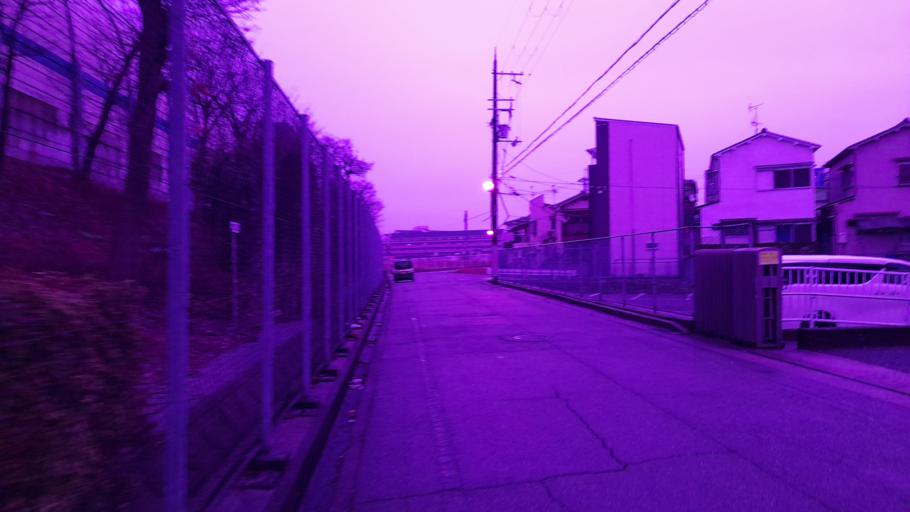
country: JP
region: Osaka
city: Toyonaka
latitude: 34.7456
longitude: 135.4506
